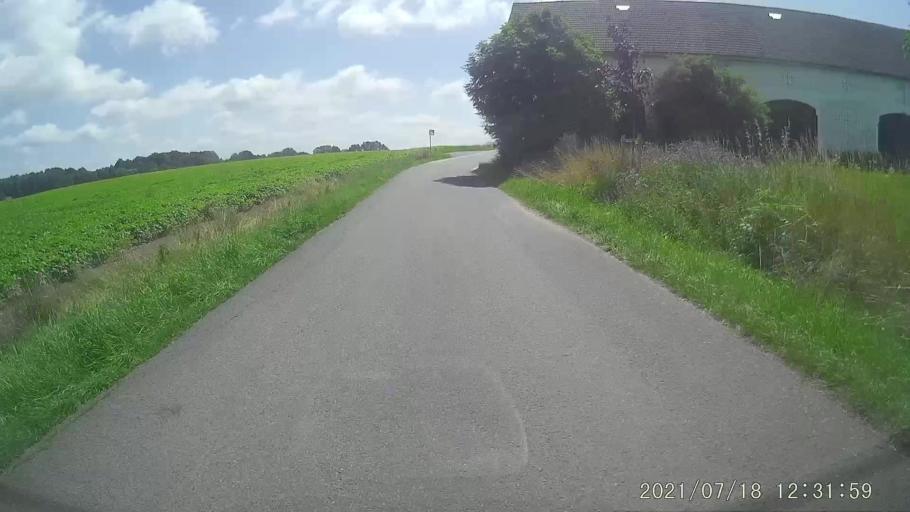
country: DE
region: Saxony
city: Konigshain
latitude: 51.1803
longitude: 14.8963
